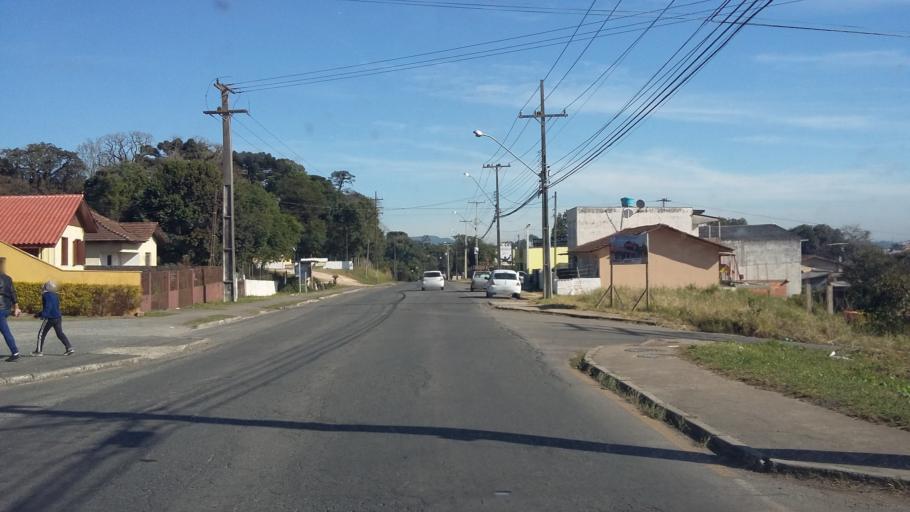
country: BR
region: Parana
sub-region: Campo Largo
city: Campo Largo
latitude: -25.4587
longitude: -49.5483
